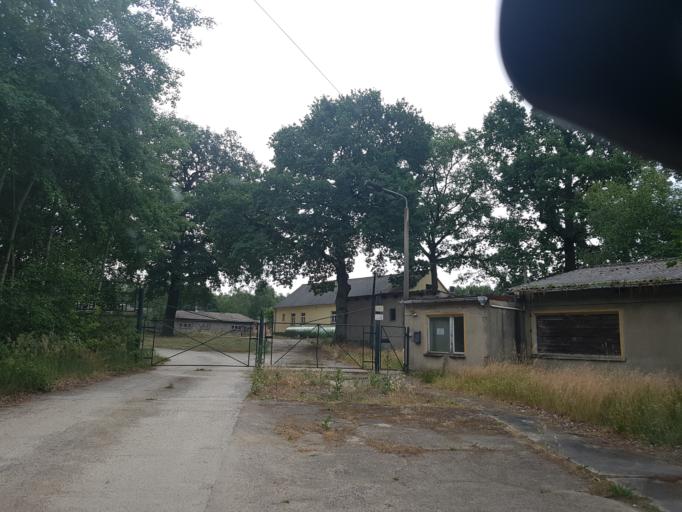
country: DE
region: Brandenburg
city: Lebusa
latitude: 51.7901
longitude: 13.4089
